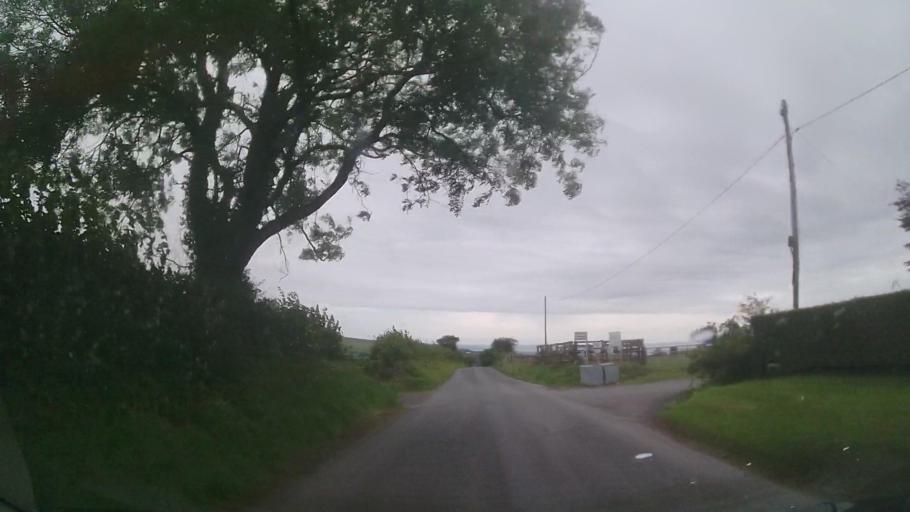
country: GB
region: Wales
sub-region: Carmarthenshire
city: Whitland
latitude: 51.7510
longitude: -4.5915
